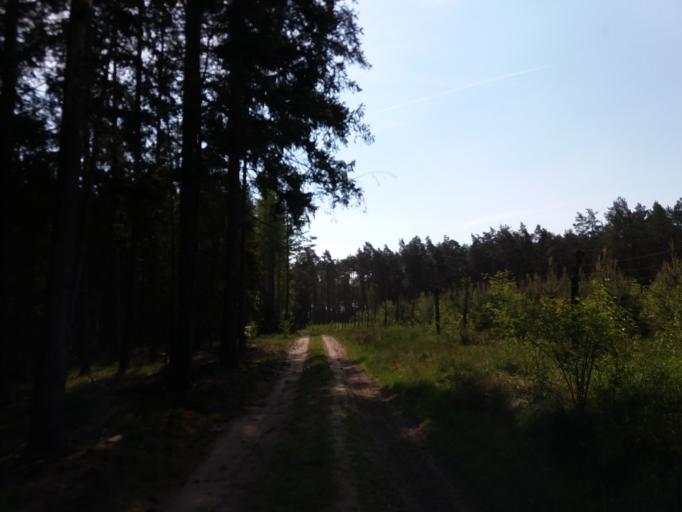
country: PL
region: West Pomeranian Voivodeship
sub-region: Powiat choszczenski
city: Bierzwnik
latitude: 53.1075
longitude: 15.6989
